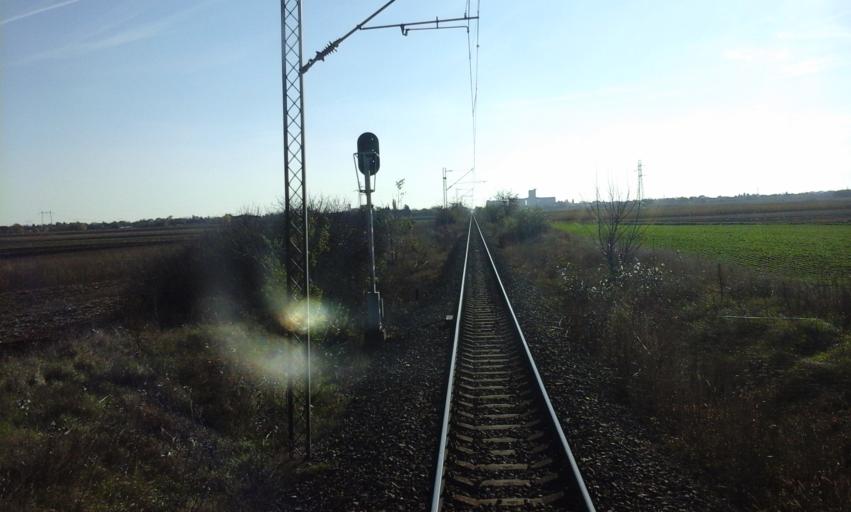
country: RS
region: Autonomna Pokrajina Vojvodina
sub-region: Severnobacki Okrug
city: Backa Topola
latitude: 45.8363
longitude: 19.6524
